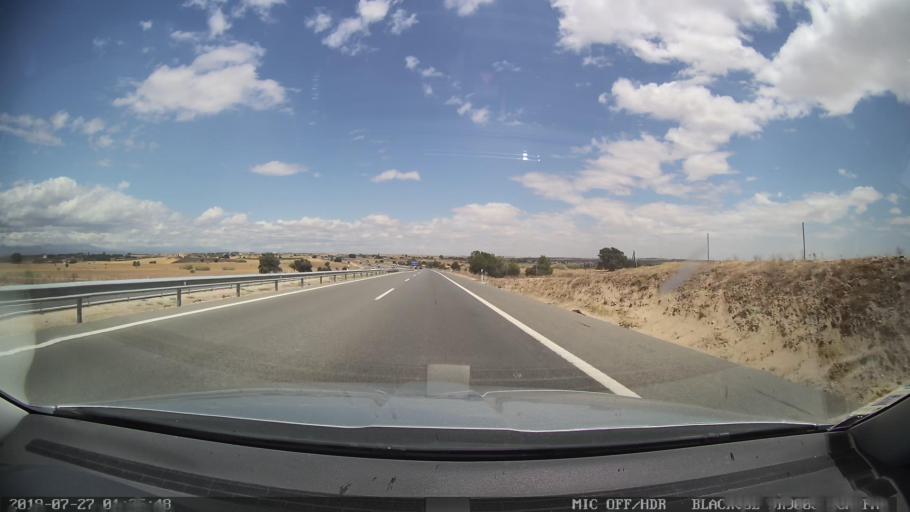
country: ES
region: Castille-La Mancha
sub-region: Province of Toledo
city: La Torre de Esteban Hambran
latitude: 40.1473
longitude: -4.1820
